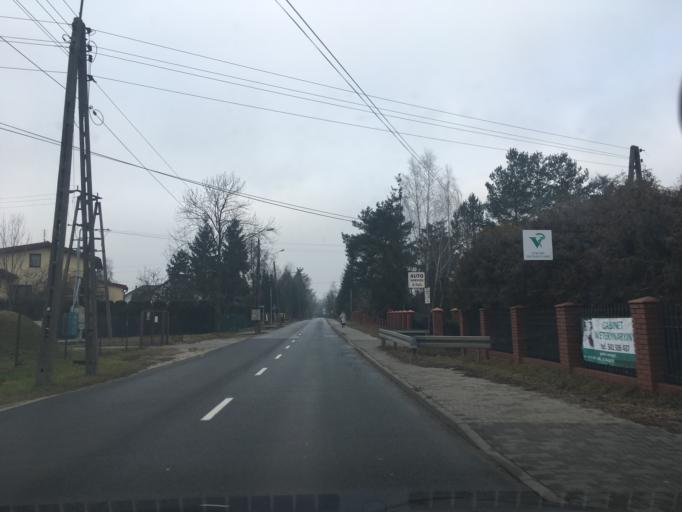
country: PL
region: Masovian Voivodeship
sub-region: Powiat piaseczynski
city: Lesznowola
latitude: 52.0334
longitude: 20.9507
